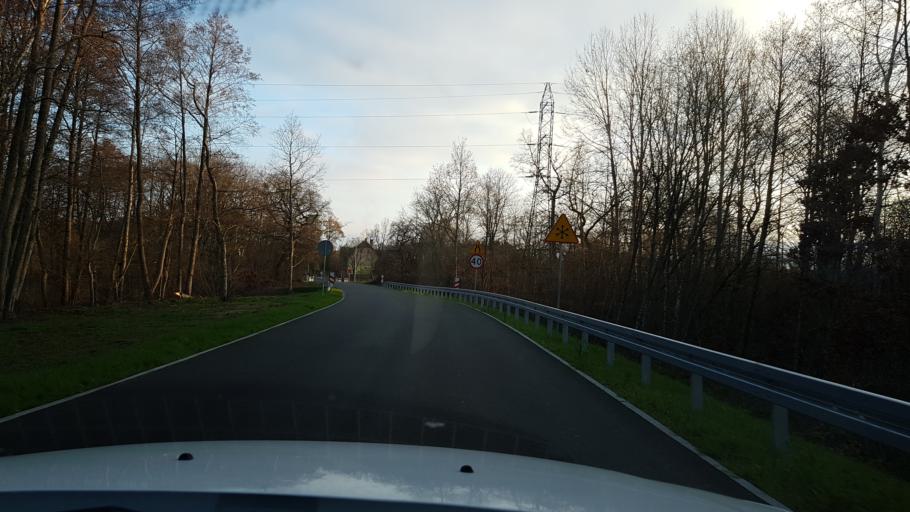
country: PL
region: West Pomeranian Voivodeship
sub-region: Koszalin
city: Koszalin
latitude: 54.1237
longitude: 16.0916
